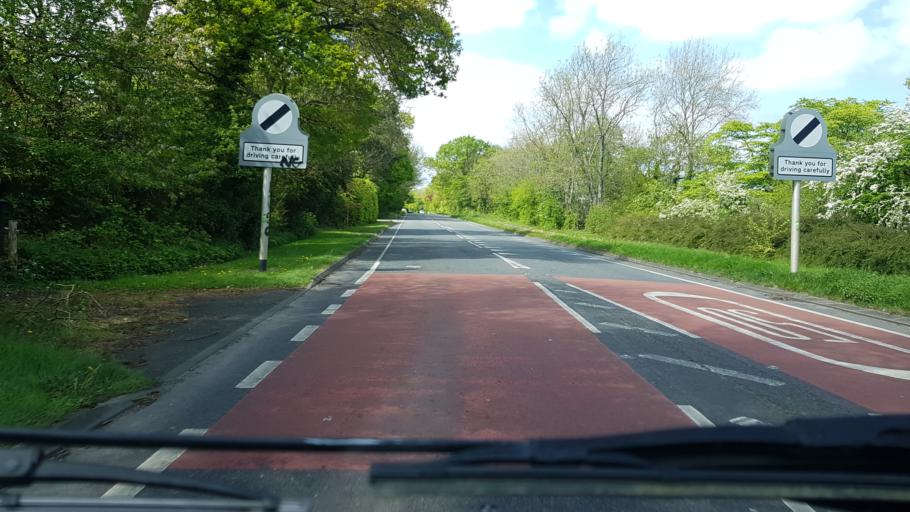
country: GB
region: England
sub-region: East Sussex
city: Robertsbridge
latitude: 51.0346
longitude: 0.4592
